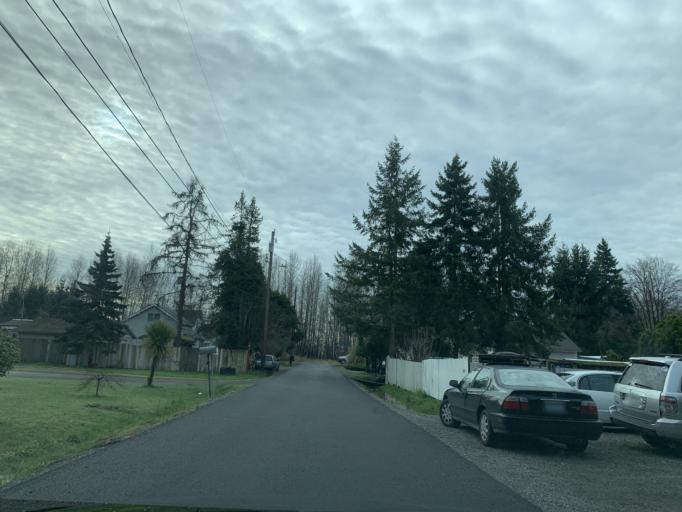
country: US
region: Washington
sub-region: Pierce County
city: Fife Heights
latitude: 47.2546
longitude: -122.3526
